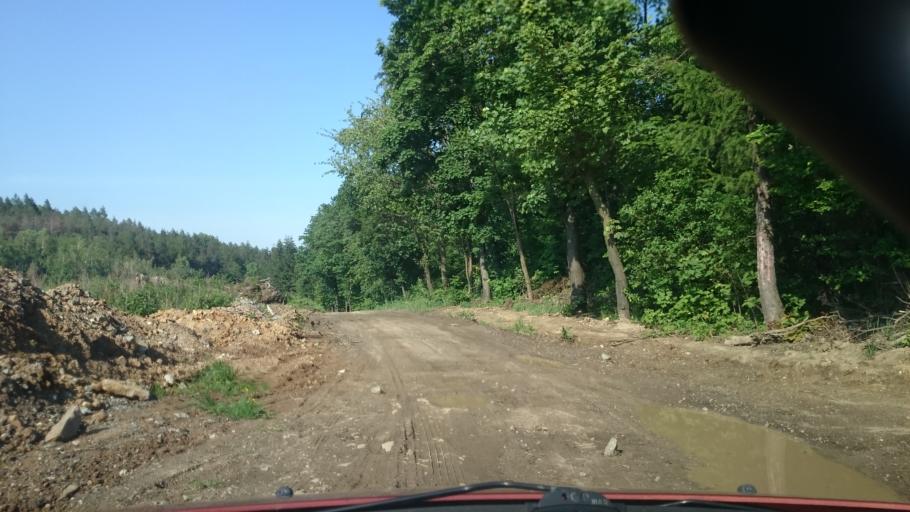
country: PL
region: Lower Silesian Voivodeship
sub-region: Powiat zabkowicki
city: Bardo
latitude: 50.5133
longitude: 16.7434
